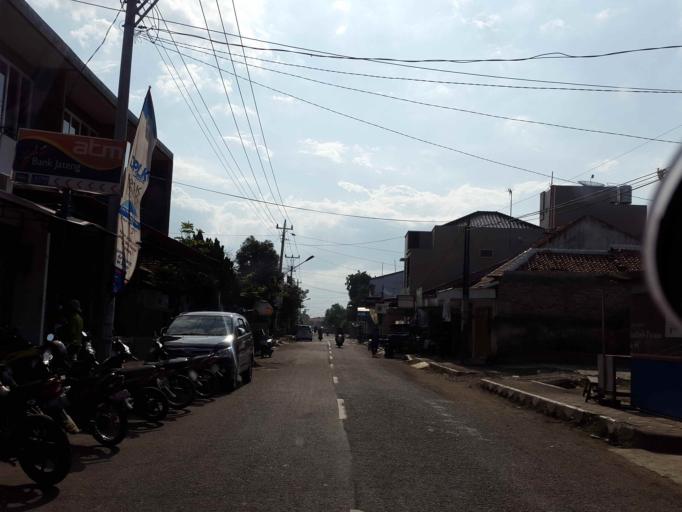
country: ID
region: Central Java
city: Pemalang
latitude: -6.8899
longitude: 109.3797
